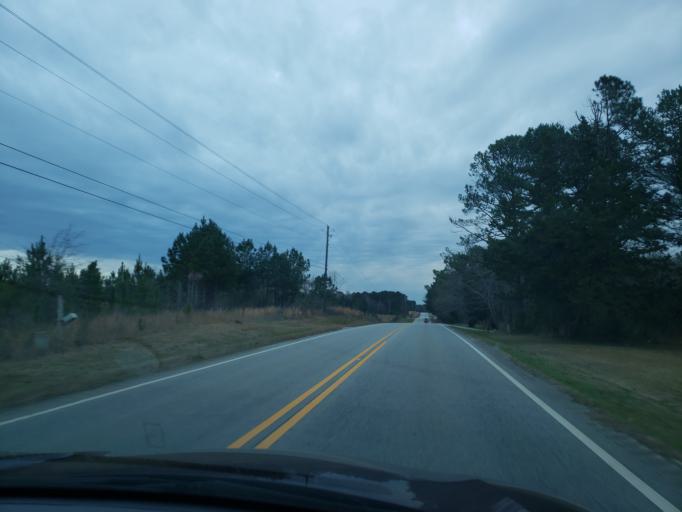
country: US
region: Alabama
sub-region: Chambers County
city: Lafayette
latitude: 32.9990
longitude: -85.3759
